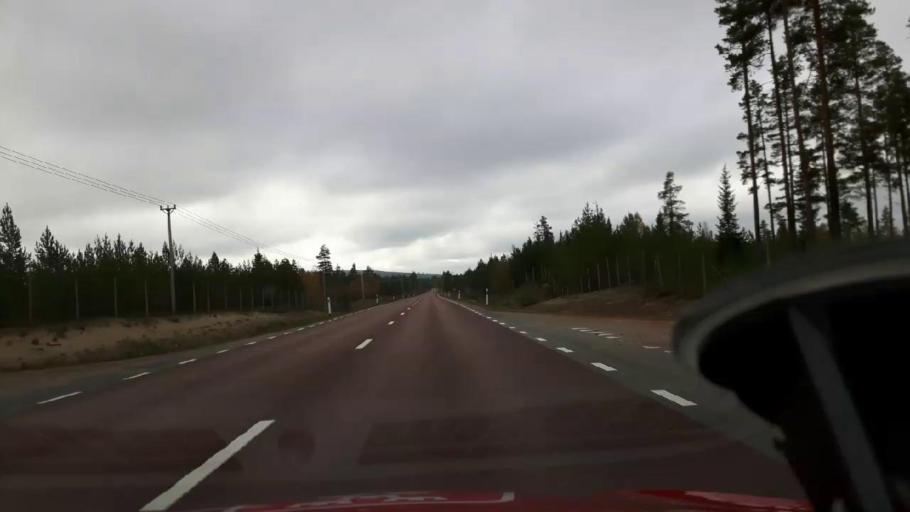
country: SE
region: Jaemtland
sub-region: Harjedalens Kommun
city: Sveg
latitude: 62.2313
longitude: 14.8405
